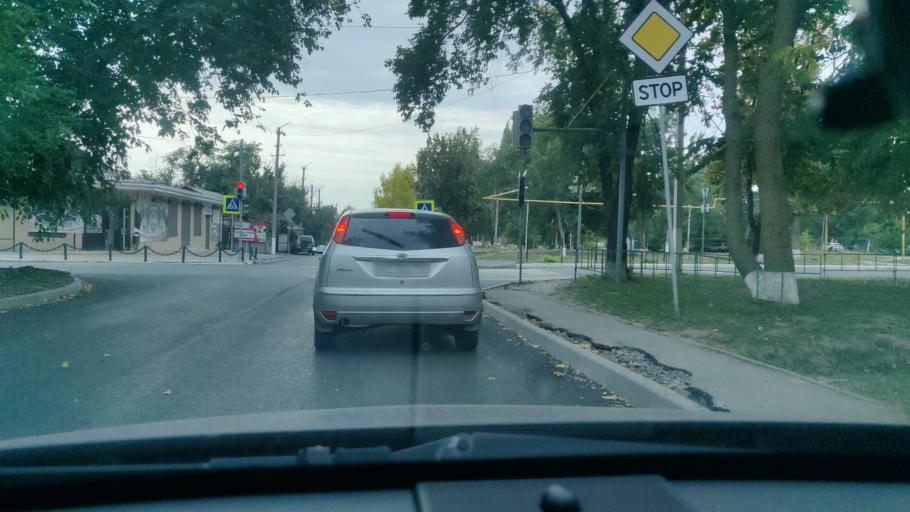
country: RU
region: Rostov
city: Ust'-Donetskiy
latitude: 47.6418
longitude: 40.8731
